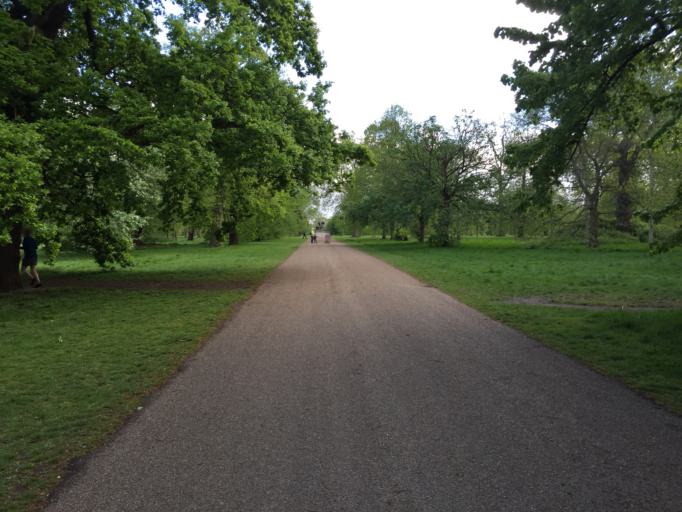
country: GB
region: England
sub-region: Greater London
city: Bayswater
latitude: 51.5083
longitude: -0.1774
